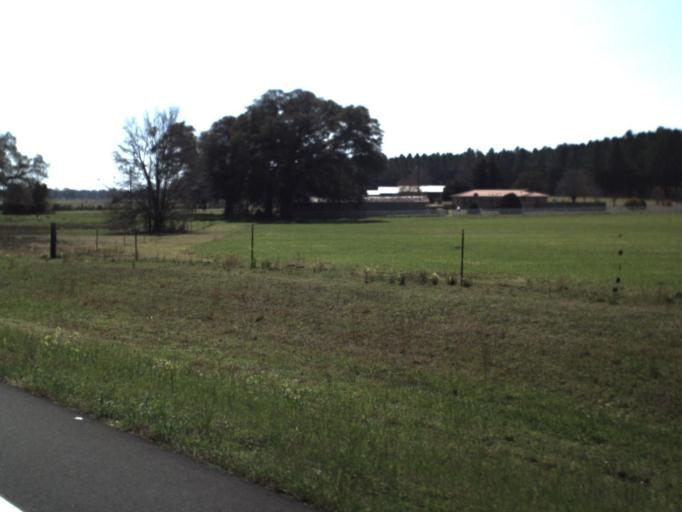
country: US
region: Florida
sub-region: Jackson County
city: Sneads
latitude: 30.8059
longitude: -85.0357
